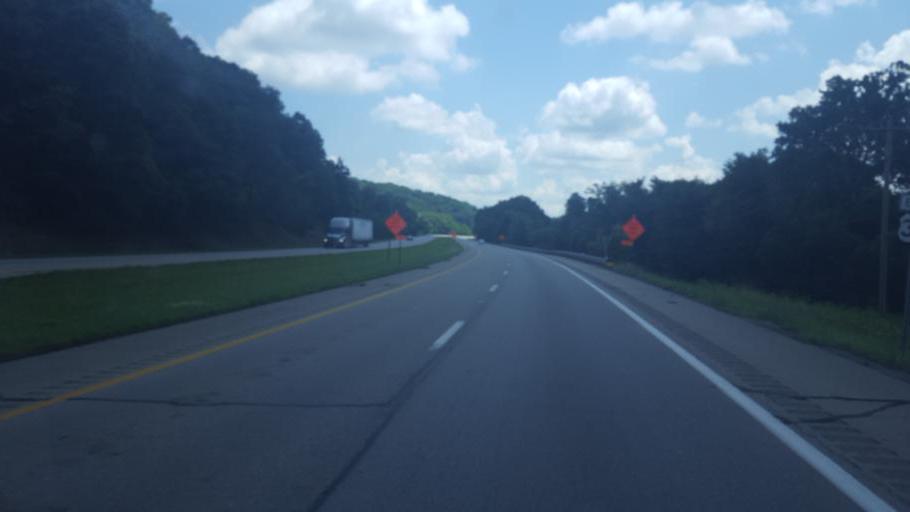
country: US
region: Ohio
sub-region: Jackson County
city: Jackson
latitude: 39.1331
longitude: -82.7125
